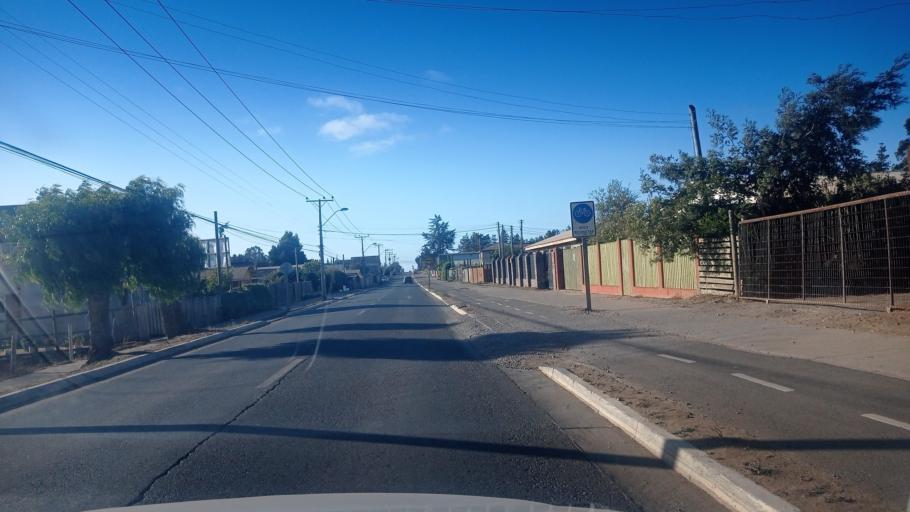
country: CL
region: O'Higgins
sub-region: Provincia de Colchagua
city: Santa Cruz
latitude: -34.4073
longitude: -71.9956
